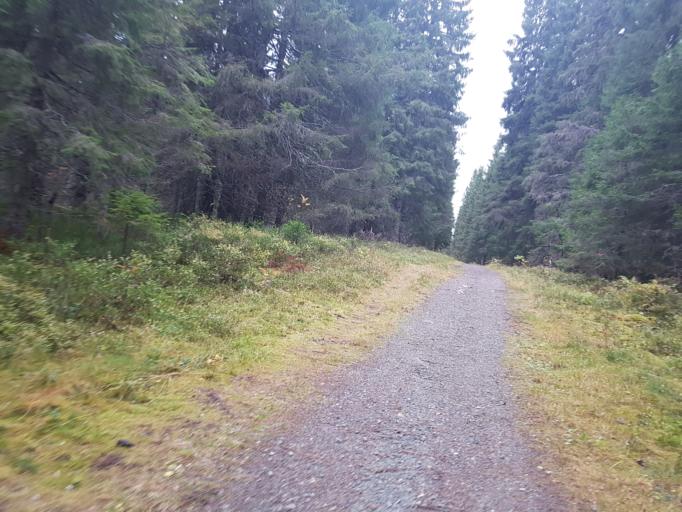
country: NO
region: Sor-Trondelag
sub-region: Melhus
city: Melhus
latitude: 63.3812
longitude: 10.2544
